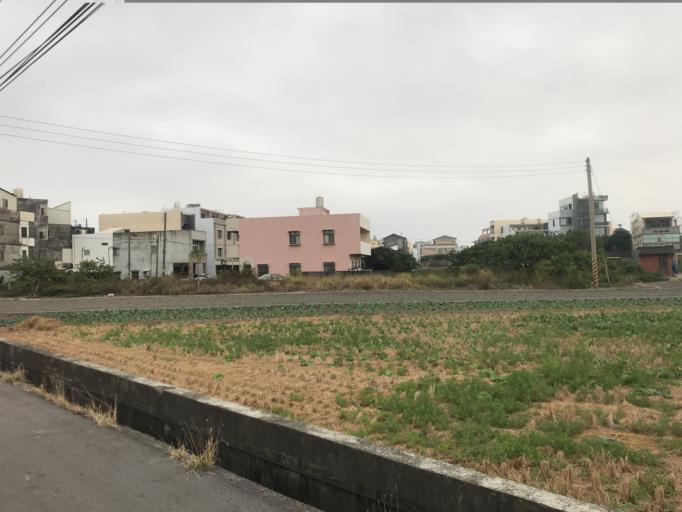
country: TW
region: Taiwan
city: Fengyuan
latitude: 24.3597
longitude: 120.6042
